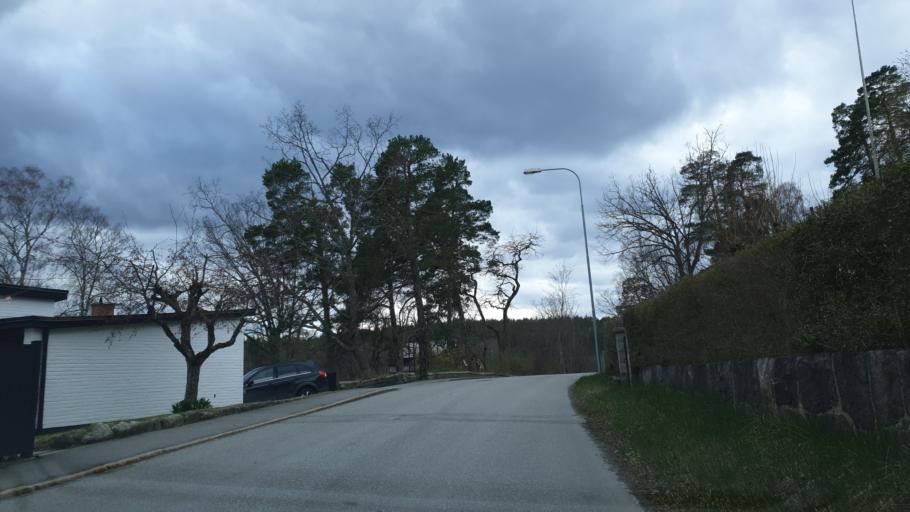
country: SE
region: Stockholm
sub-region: Nacka Kommun
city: Nacka
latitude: 59.3018
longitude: 18.2020
